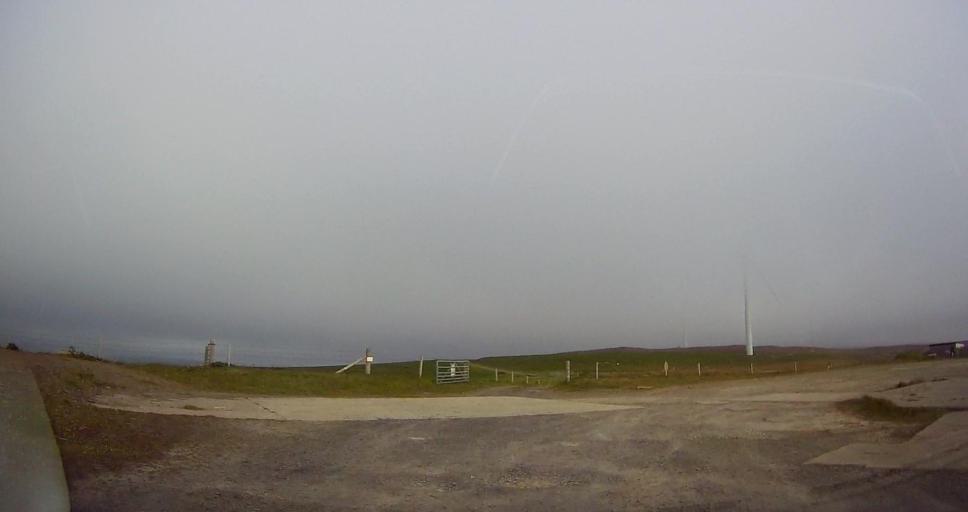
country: GB
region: Scotland
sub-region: Orkney Islands
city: Stromness
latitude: 59.1151
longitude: -3.1461
